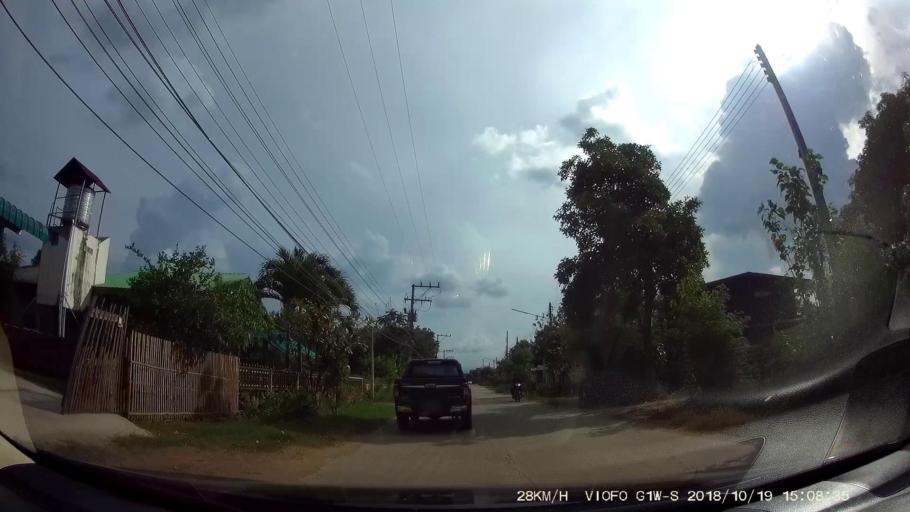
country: TH
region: Chaiyaphum
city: Phu Khiao
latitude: 16.4134
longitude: 102.1037
